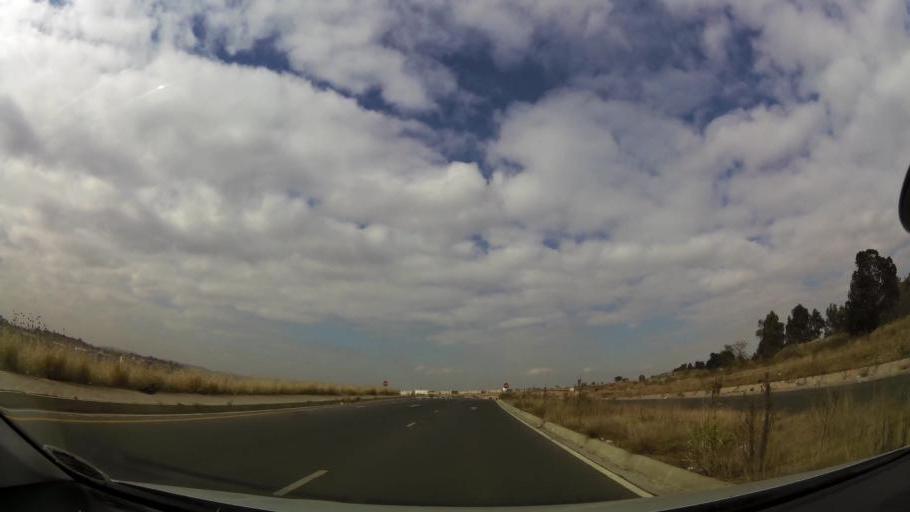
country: ZA
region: Gauteng
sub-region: City of Johannesburg Metropolitan Municipality
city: Roodepoort
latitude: -26.2015
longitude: 27.9040
